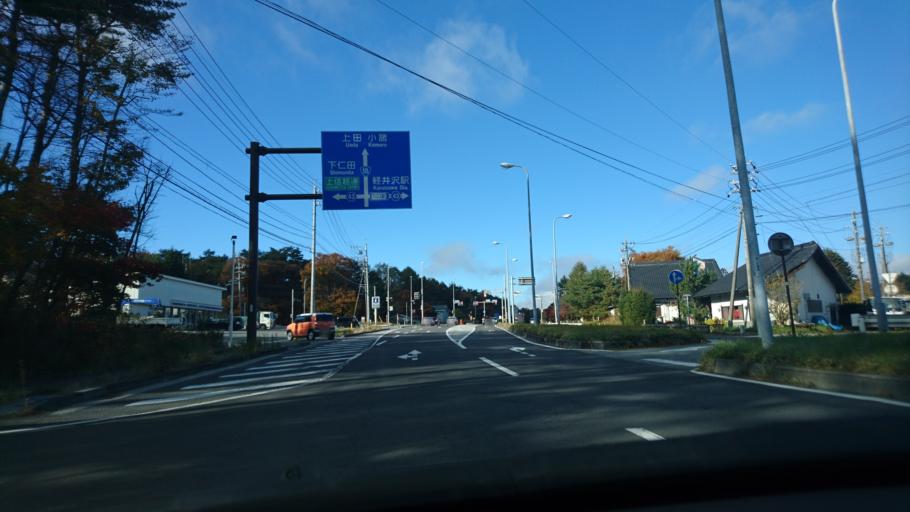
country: JP
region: Nagano
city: Saku
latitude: 36.3243
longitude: 138.6297
